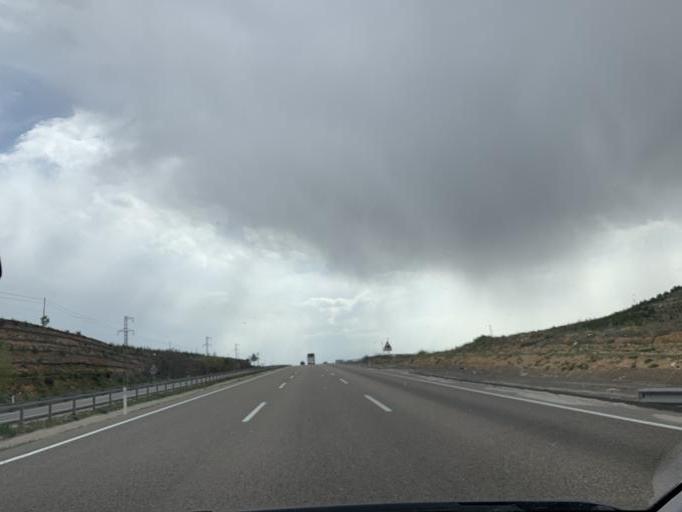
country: TR
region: Eskisehir
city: Sivrihisar
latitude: 39.5102
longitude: 31.6135
